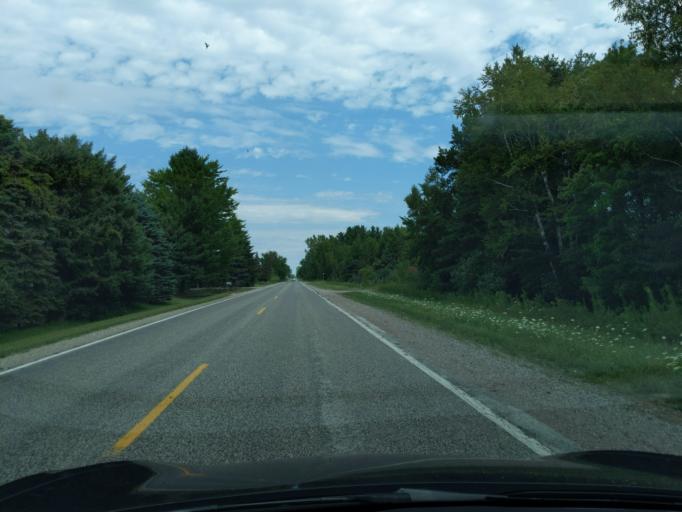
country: US
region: Michigan
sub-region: Gratiot County
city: Breckenridge
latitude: 43.4322
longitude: -84.3700
